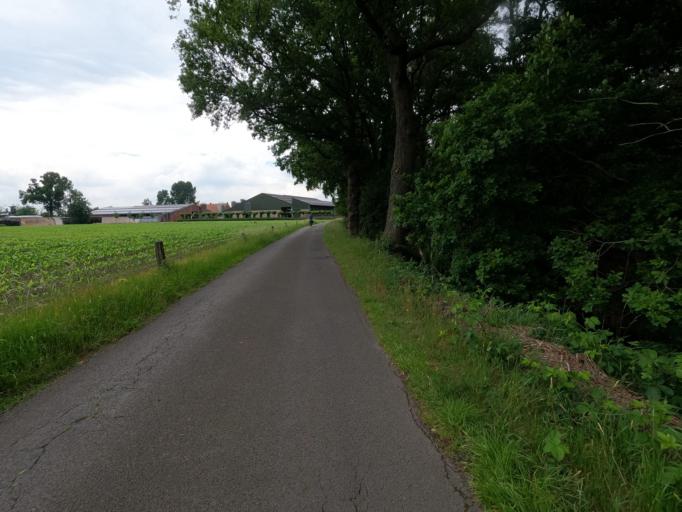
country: BE
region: Flanders
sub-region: Provincie Antwerpen
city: Essen
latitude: 51.4559
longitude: 4.5078
